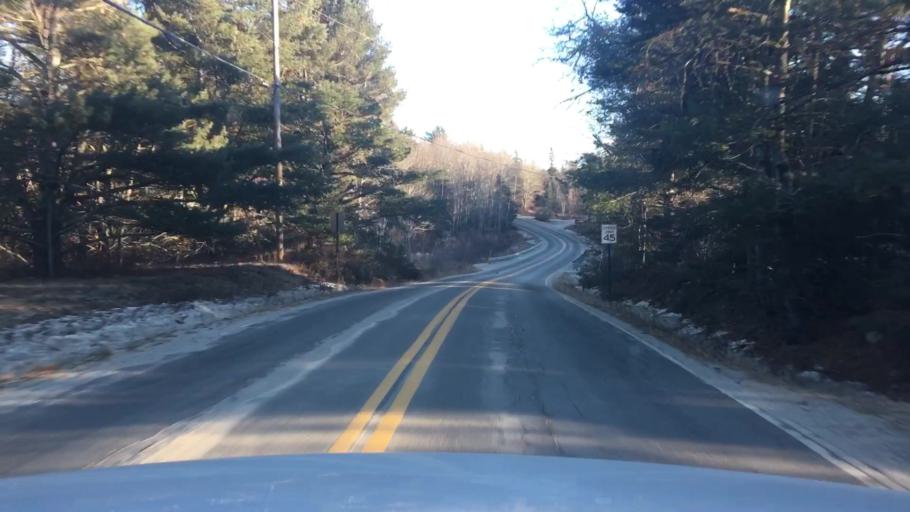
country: US
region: Maine
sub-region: Hancock County
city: Penobscot
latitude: 44.3882
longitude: -68.6979
